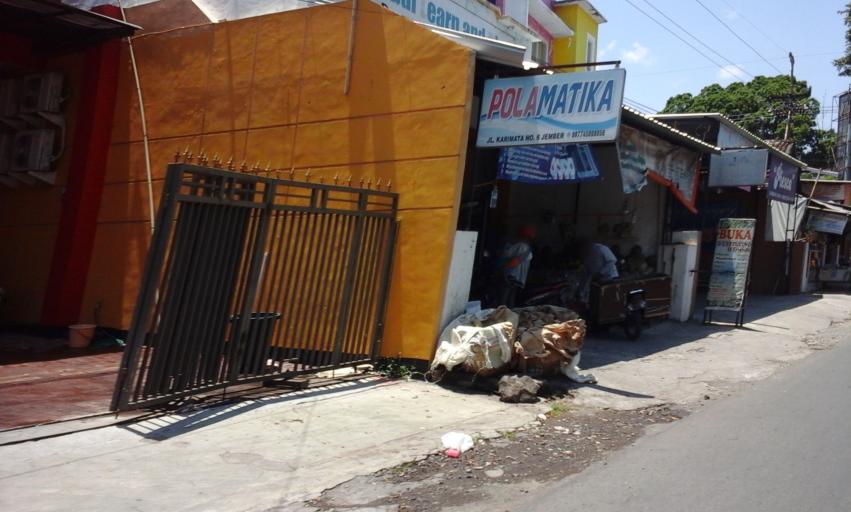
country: ID
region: East Java
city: Sumbersari Wetan
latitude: -8.1814
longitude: 113.7153
